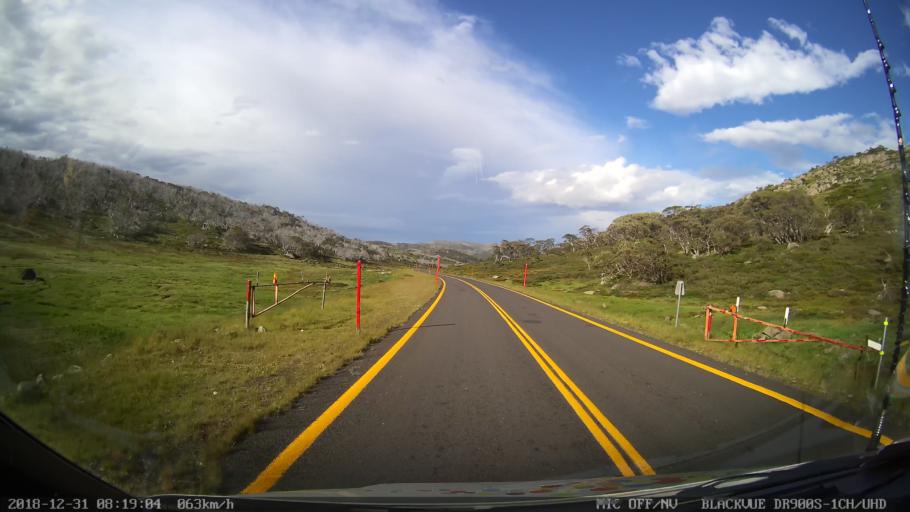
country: AU
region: New South Wales
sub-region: Snowy River
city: Jindabyne
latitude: -36.4171
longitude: 148.3899
